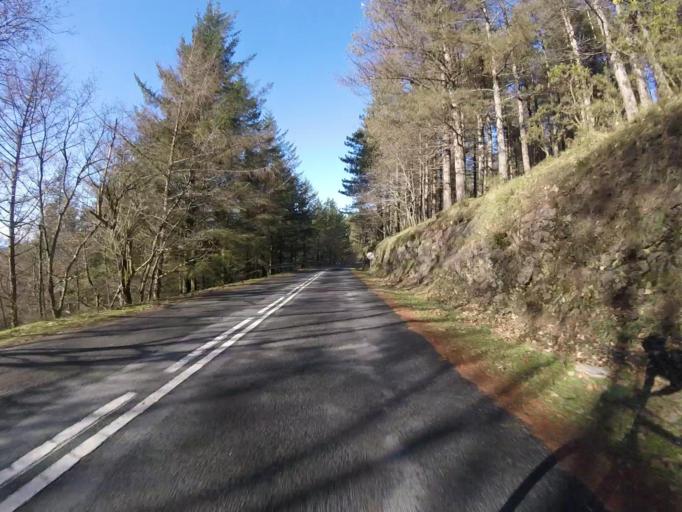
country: ES
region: Basque Country
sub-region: Provincia de Guipuzcoa
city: Irun
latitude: 43.2962
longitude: -1.7887
